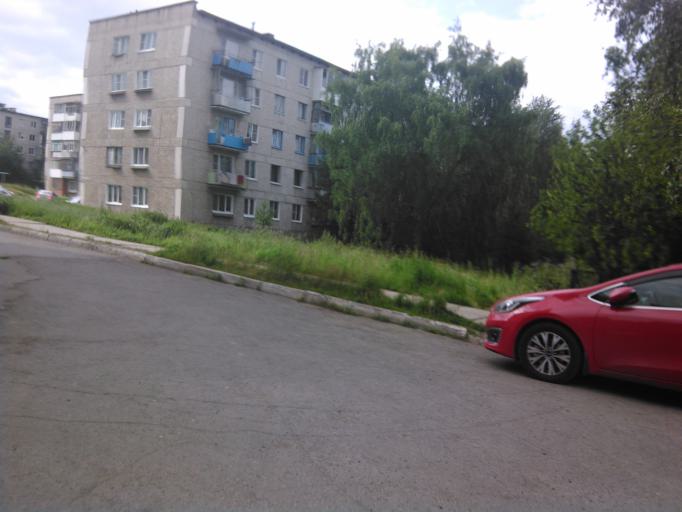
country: RU
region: Sverdlovsk
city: Krasnotur'insk
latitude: 59.7590
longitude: 60.1630
